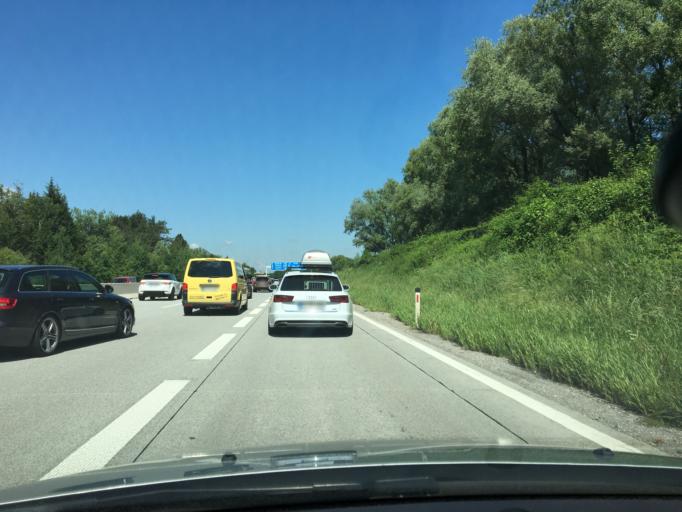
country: AT
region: Salzburg
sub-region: Politischer Bezirk Salzburg-Umgebung
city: Grodig
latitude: 47.7594
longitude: 13.0039
